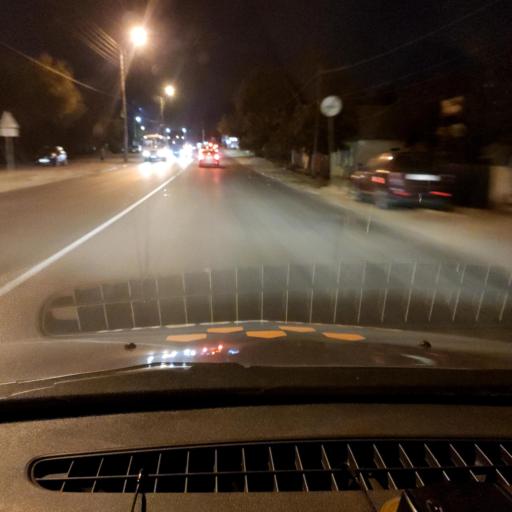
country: RU
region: Voronezj
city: Voronezh
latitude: 51.6339
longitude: 39.1732
